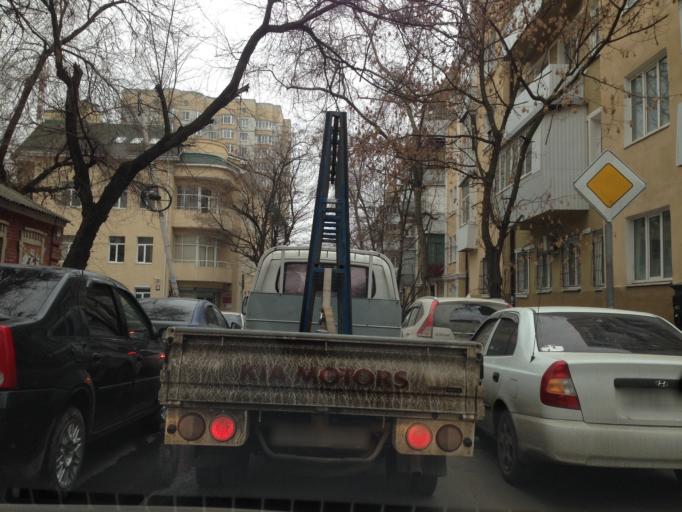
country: RU
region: Rostov
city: Rostov-na-Donu
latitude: 47.2303
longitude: 39.7063
